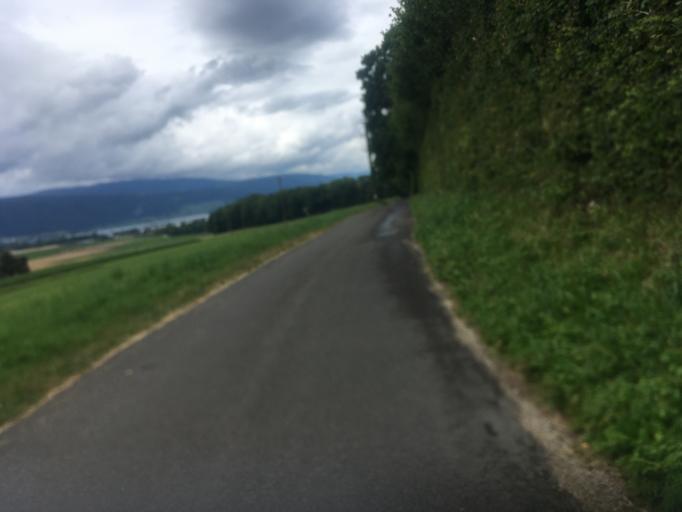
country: CH
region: Bern
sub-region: Seeland District
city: Ins
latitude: 47.0159
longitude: 7.0991
